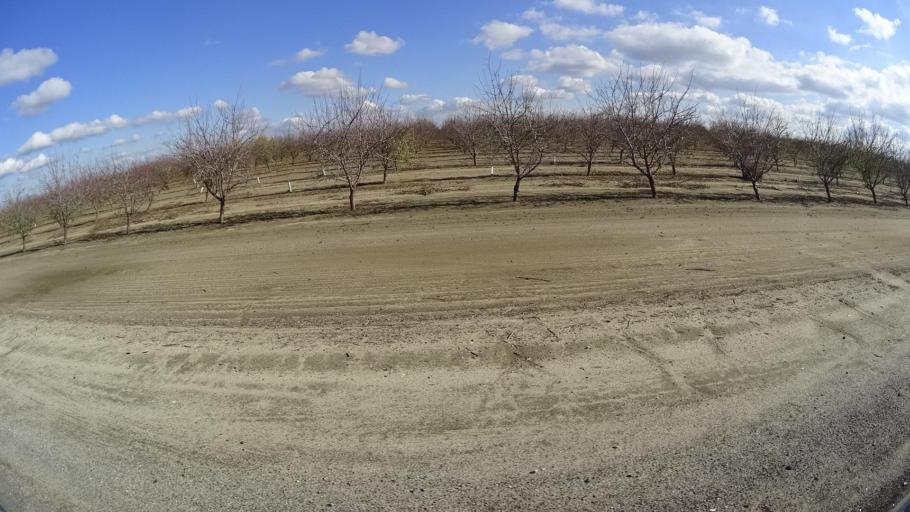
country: US
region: California
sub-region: Kern County
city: Delano
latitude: 35.7275
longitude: -119.2584
